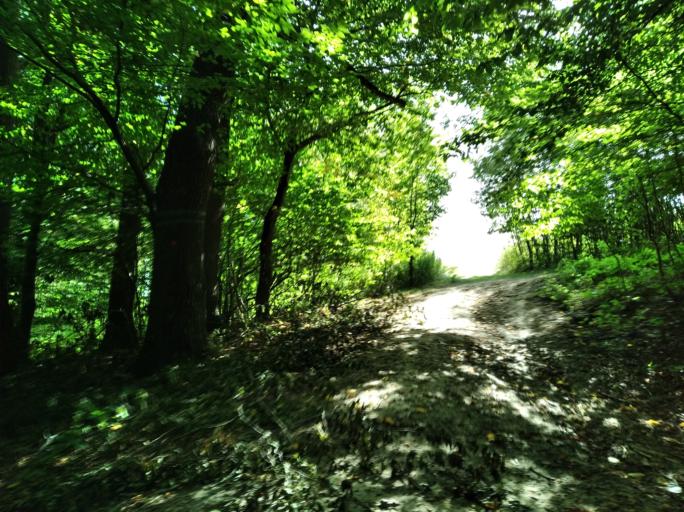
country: PL
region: Subcarpathian Voivodeship
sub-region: Powiat strzyzowski
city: Wisniowa
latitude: 49.8777
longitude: 21.6258
